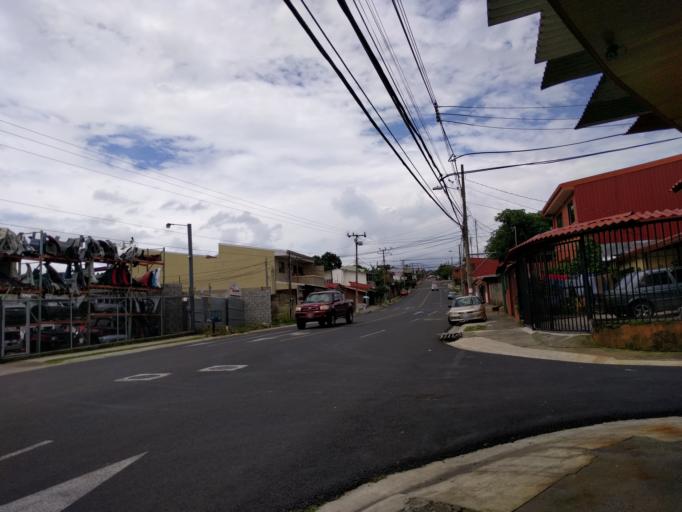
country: CR
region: Heredia
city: Llorente
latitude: 9.9930
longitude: -84.1507
